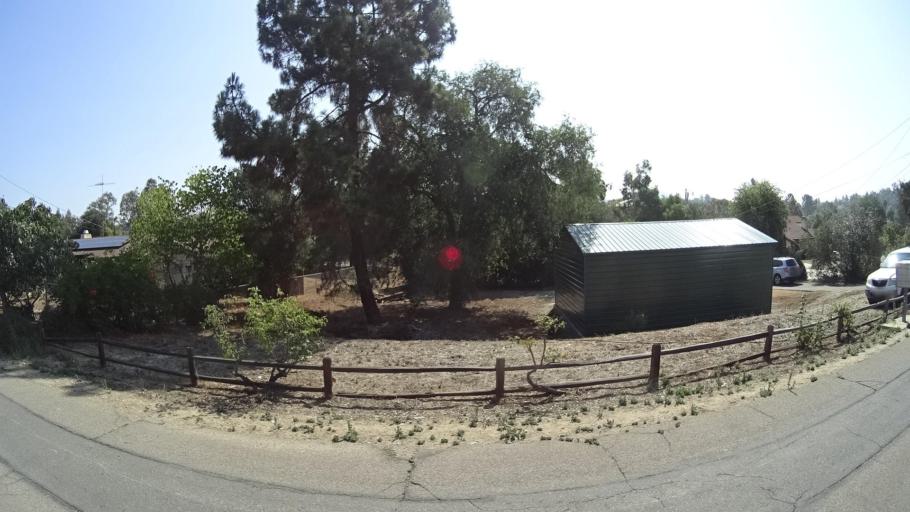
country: US
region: California
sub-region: San Diego County
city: Vista
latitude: 33.2353
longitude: -117.2411
